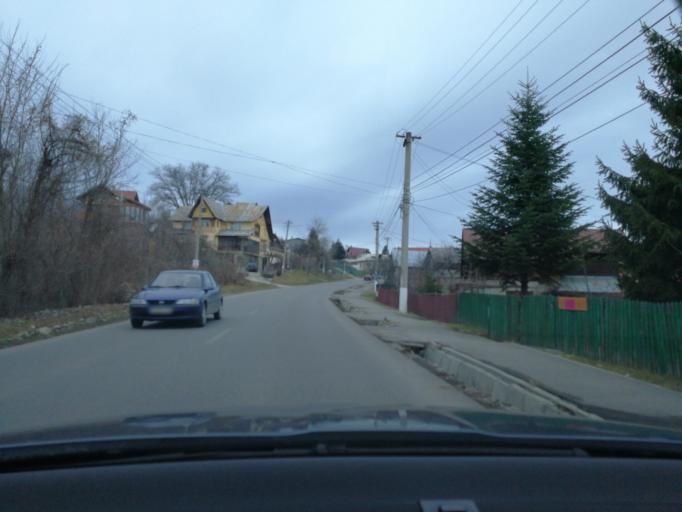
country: RO
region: Prahova
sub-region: Comuna Cornu
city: Cornu de Jos
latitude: 45.1539
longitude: 25.6887
